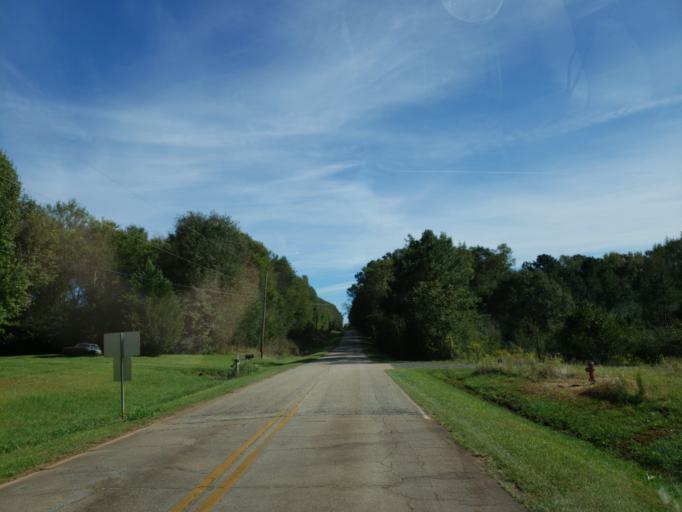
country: US
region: Georgia
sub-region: Crawford County
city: Roberta
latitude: 32.8582
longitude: -84.0864
